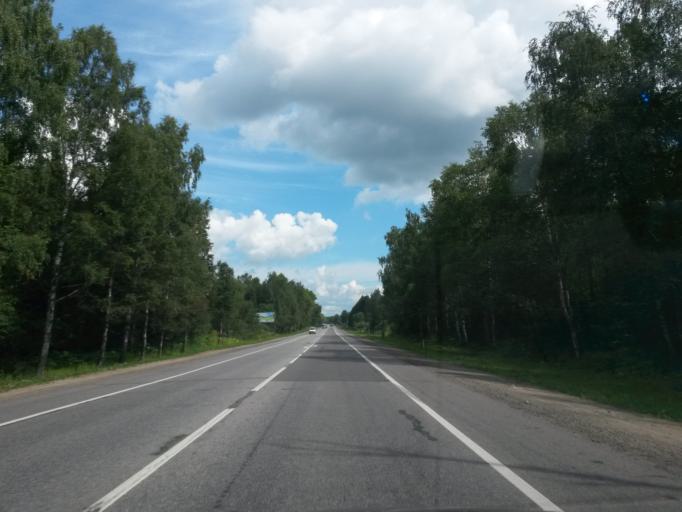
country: RU
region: Jaroslavl
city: Pereslavl'-Zalesskiy
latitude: 56.6808
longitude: 38.7368
